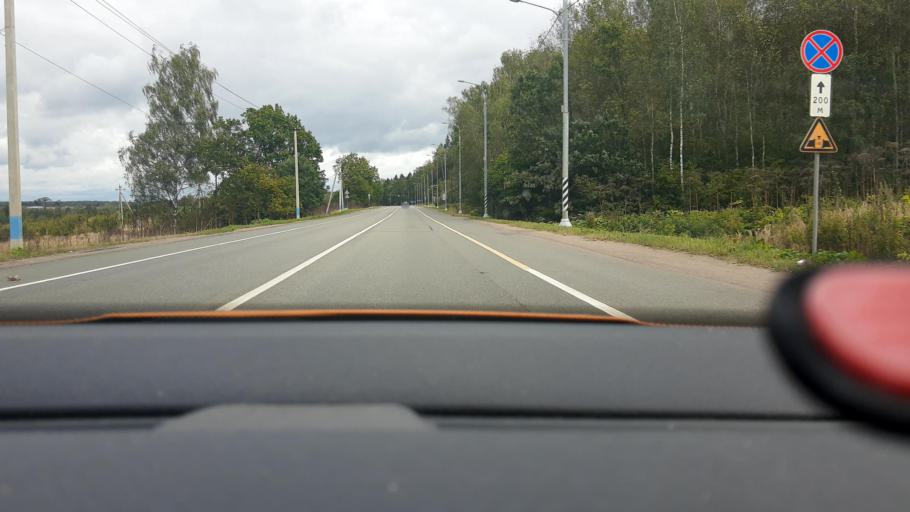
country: RU
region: Moskovskaya
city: Kostino
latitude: 56.0279
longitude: 37.9570
